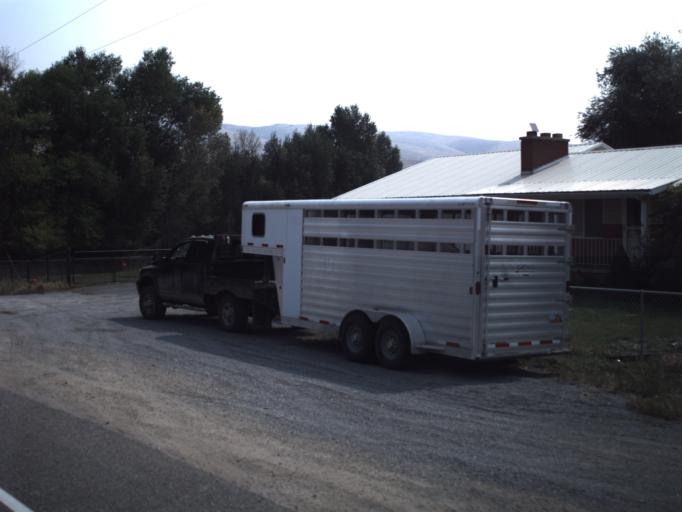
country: US
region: Utah
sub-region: Summit County
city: Coalville
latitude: 41.0149
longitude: -111.4925
